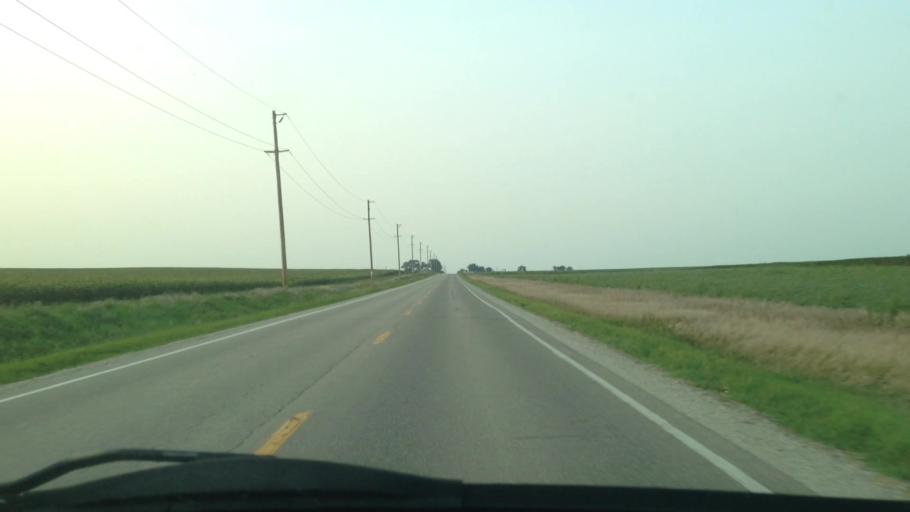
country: US
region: Iowa
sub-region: Iowa County
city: Marengo
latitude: 41.9532
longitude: -92.0852
